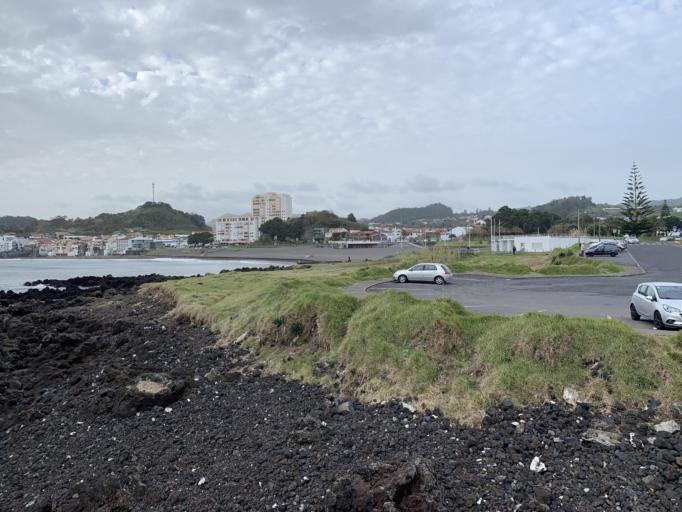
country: PT
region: Azores
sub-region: Ponta Delgada
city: Rosto de Cao
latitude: 37.7494
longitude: -25.6217
